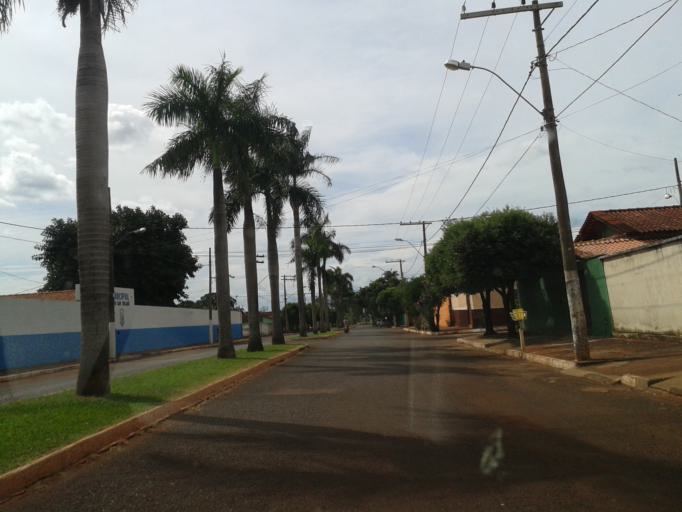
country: BR
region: Minas Gerais
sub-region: Centralina
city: Centralina
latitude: -18.5897
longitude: -49.2005
